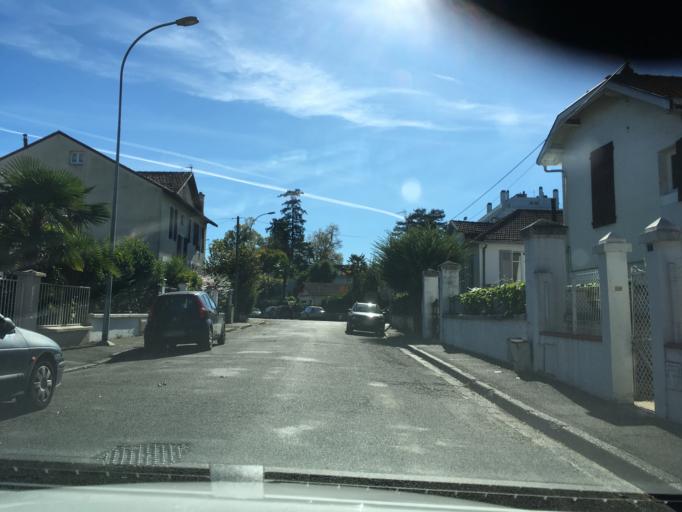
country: FR
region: Aquitaine
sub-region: Departement des Pyrenees-Atlantiques
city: Pau
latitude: 43.3073
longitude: -0.3670
